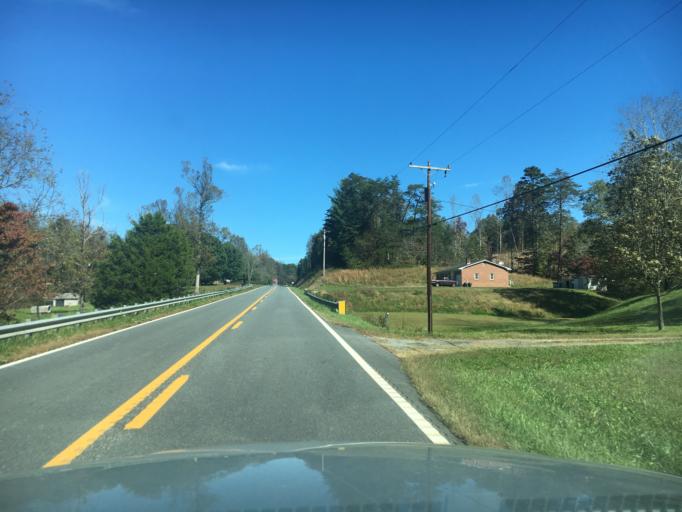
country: US
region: North Carolina
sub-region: Rutherford County
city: Spindale
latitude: 35.4933
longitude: -81.8662
